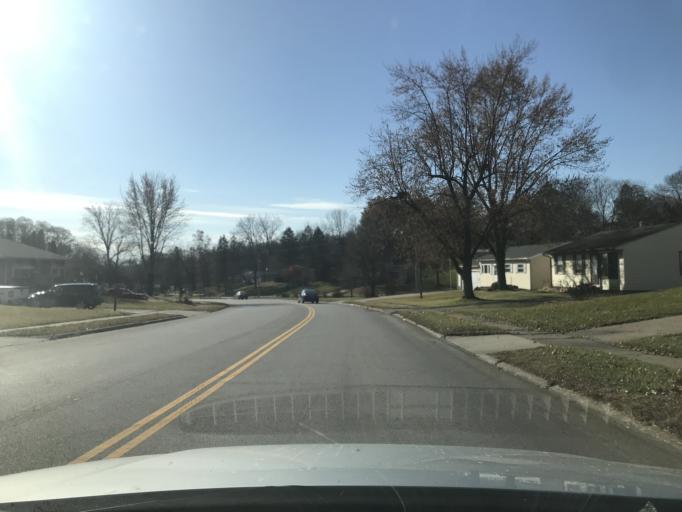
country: US
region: Iowa
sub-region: Scott County
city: Davenport
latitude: 41.5289
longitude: -90.6155
